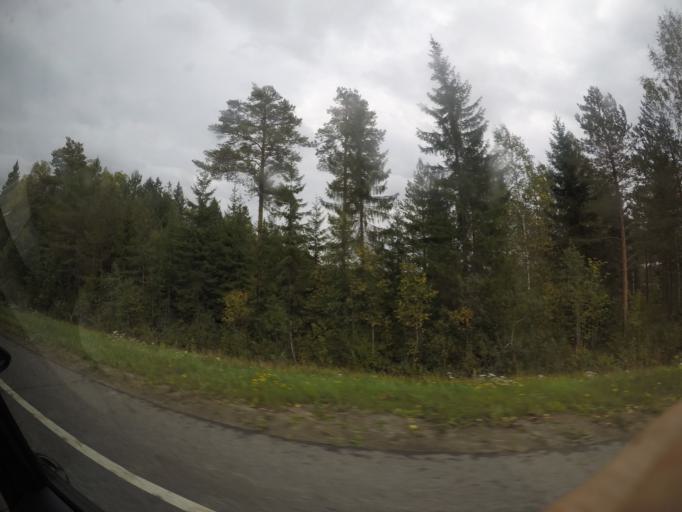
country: FI
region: Haeme
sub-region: Haemeenlinna
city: Parola
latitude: 61.1417
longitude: 24.4146
